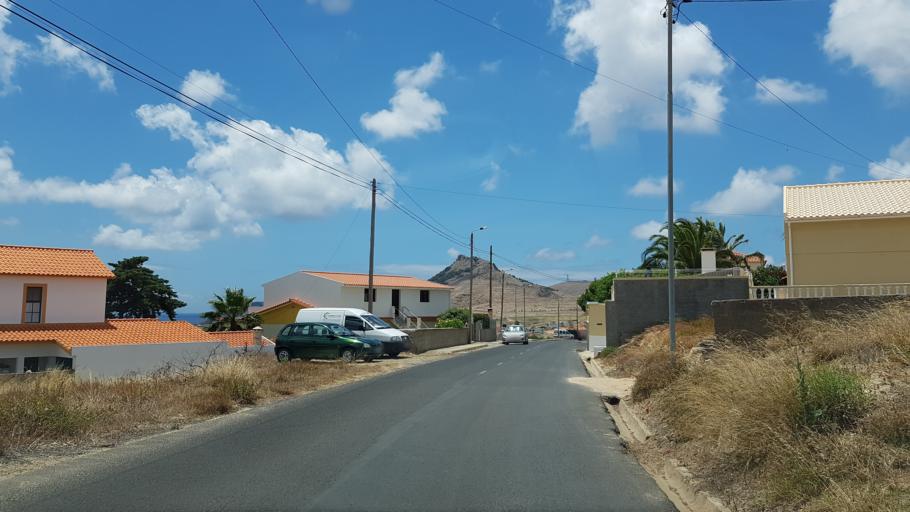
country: PT
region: Madeira
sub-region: Porto Santo
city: Vila de Porto Santo
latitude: 33.0615
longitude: -16.3530
